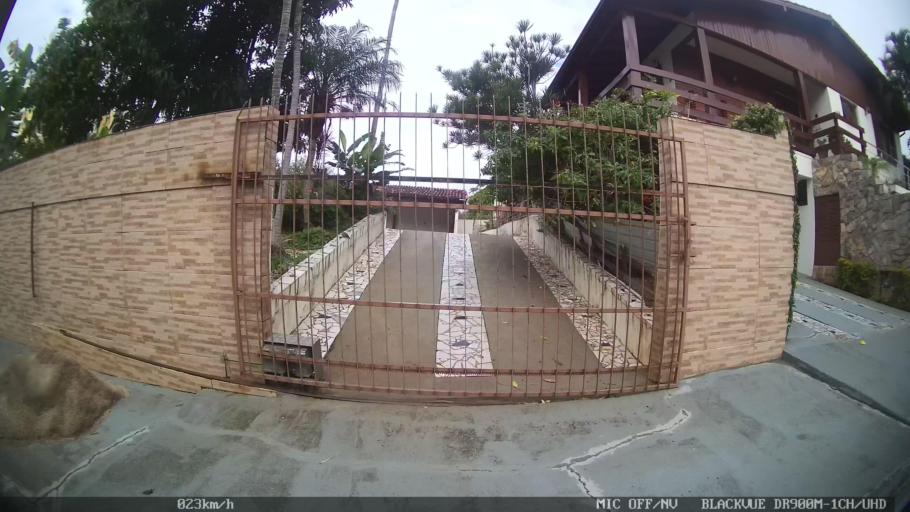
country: BR
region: Santa Catarina
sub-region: Sao Jose
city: Campinas
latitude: -27.5697
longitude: -48.6107
